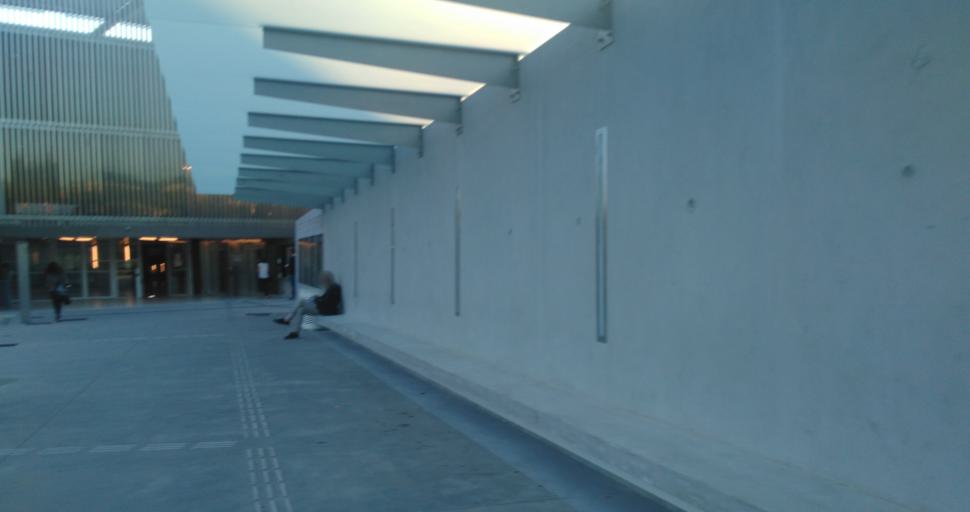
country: FR
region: Provence-Alpes-Cote d'Azur
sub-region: Departement des Bouches-du-Rhone
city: Aix-en-Provence
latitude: 43.5115
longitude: 5.4486
